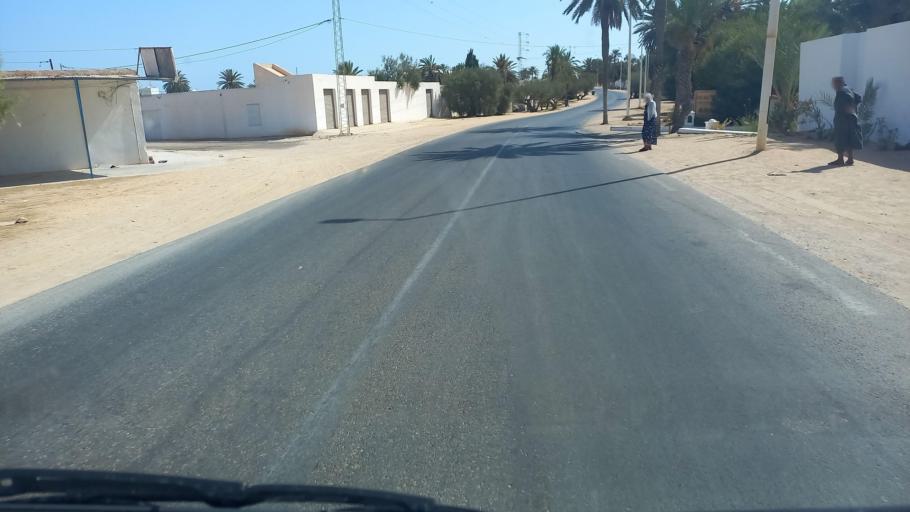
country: TN
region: Madanin
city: Midoun
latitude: 33.7812
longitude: 11.0476
